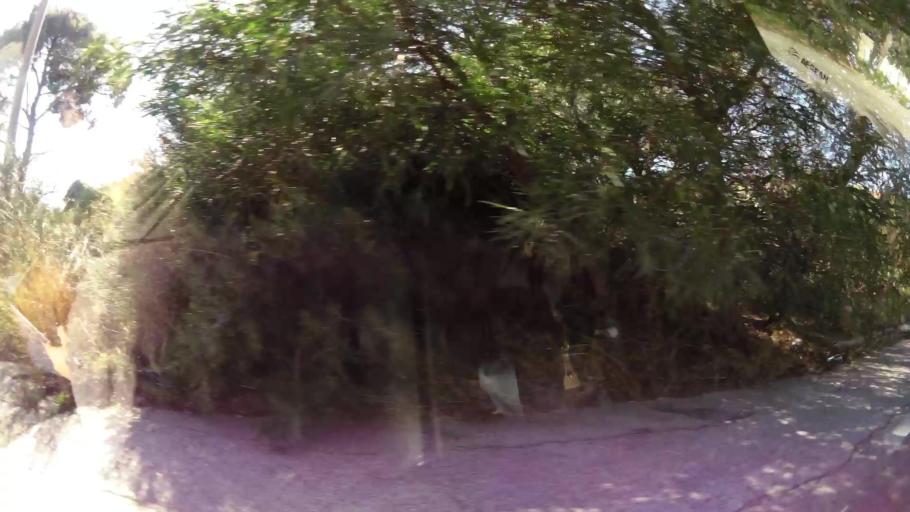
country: GR
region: Attica
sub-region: Nomarchia Anatolikis Attikis
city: Dhrafi
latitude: 38.0167
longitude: 23.9107
